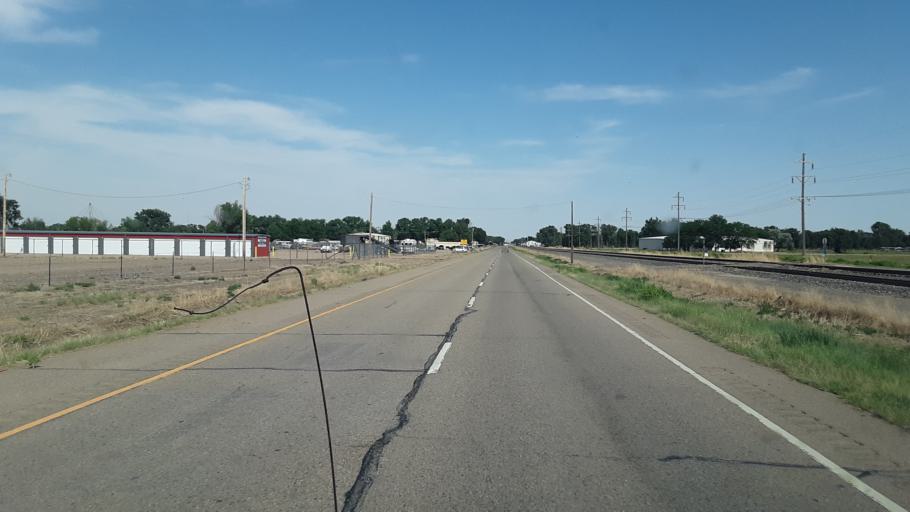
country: US
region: Colorado
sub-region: Otero County
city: Rocky Ford
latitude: 38.0614
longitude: -103.7406
